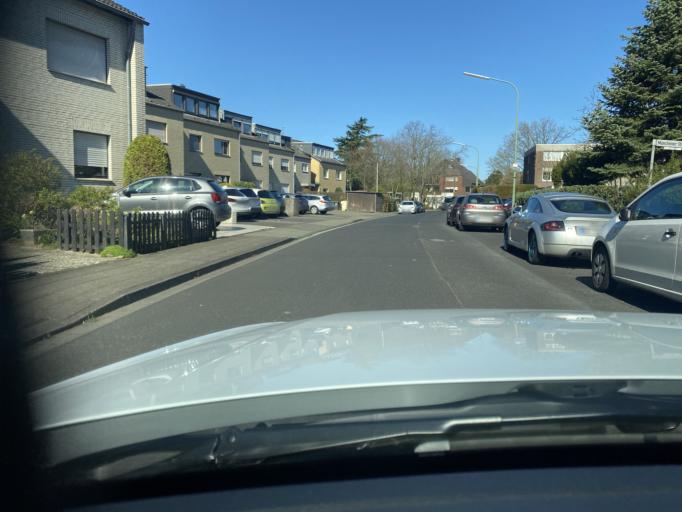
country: DE
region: North Rhine-Westphalia
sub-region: Regierungsbezirk Dusseldorf
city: Neubrueck
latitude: 51.1567
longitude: 6.6667
